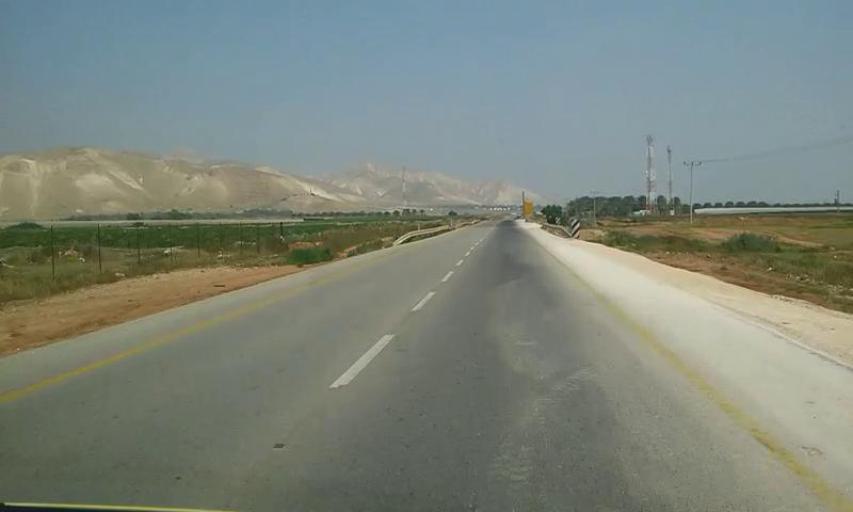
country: PS
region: West Bank
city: Al Fasayil
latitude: 32.0392
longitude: 35.4579
